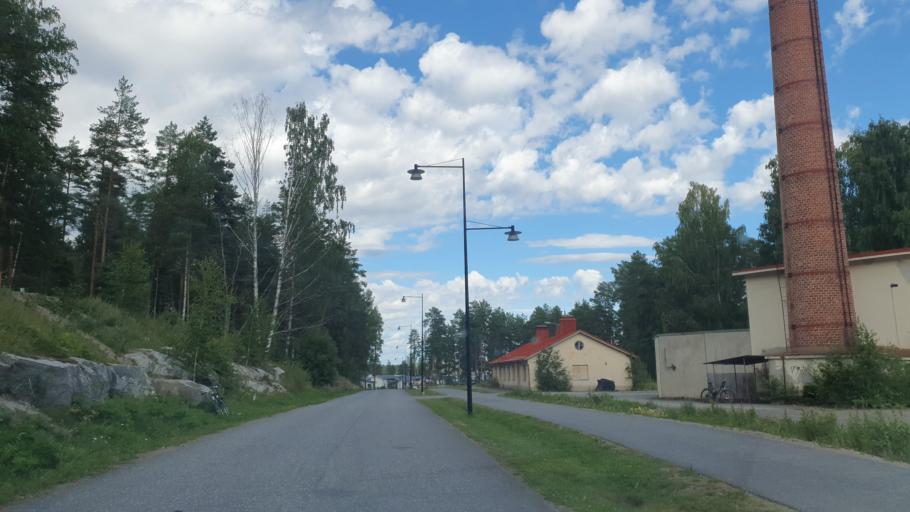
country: FI
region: Central Finland
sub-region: Jyvaeskylae
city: Saeynaetsalo
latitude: 62.1593
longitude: 25.7647
